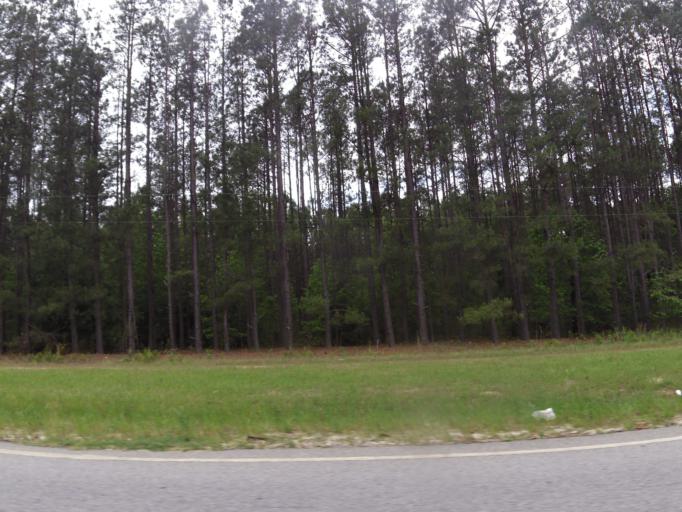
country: US
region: Georgia
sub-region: Emanuel County
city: Twin City
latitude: 32.4769
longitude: -82.2399
